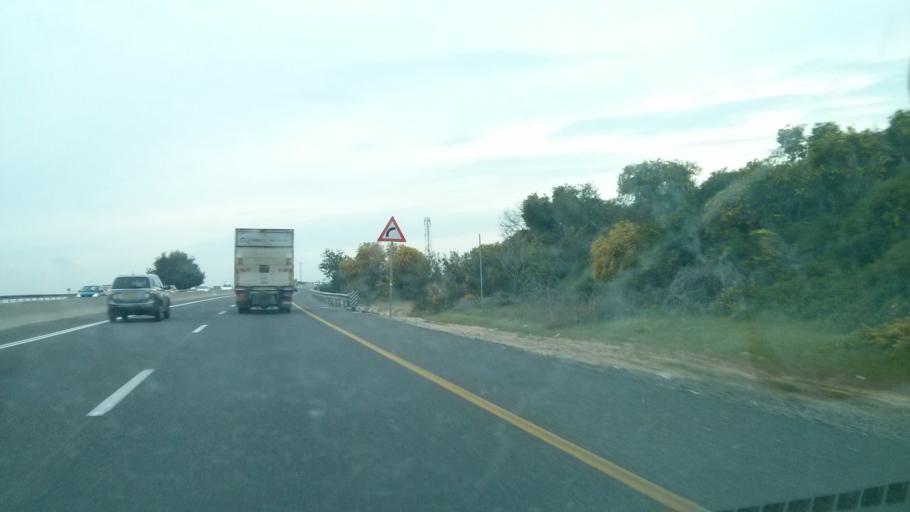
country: IL
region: Haifa
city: Qesarya
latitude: 32.4887
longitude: 34.9168
